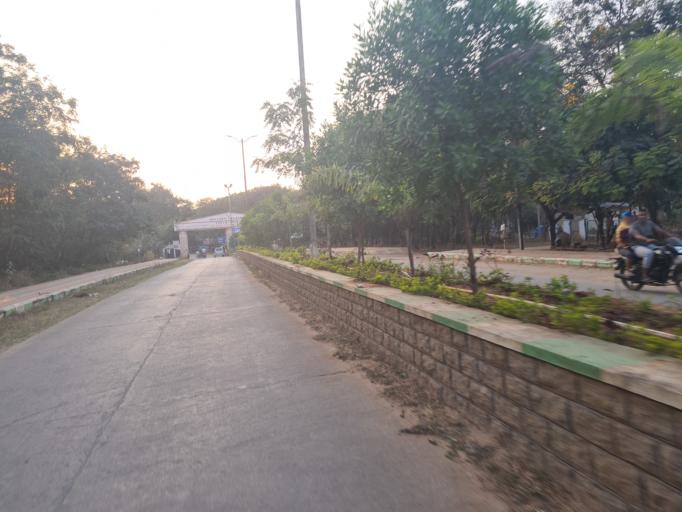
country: IN
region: Telangana
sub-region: Medak
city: Serilingampalle
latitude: 17.4780
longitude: 78.2918
